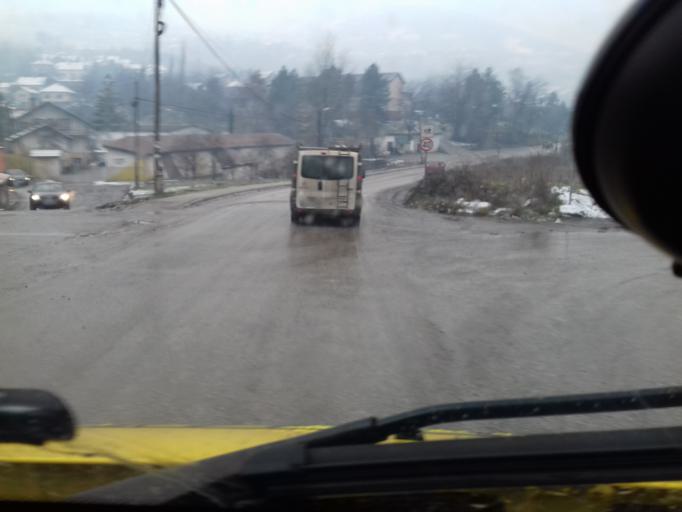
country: BA
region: Federation of Bosnia and Herzegovina
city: Zenica
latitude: 44.2306
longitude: 17.8888
